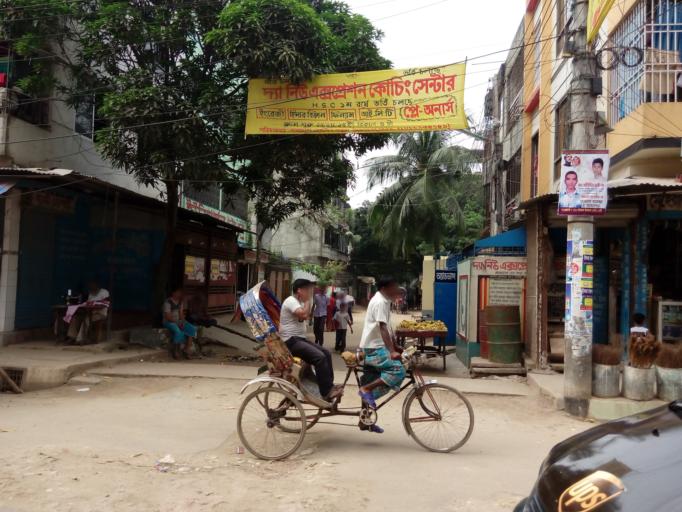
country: BD
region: Dhaka
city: Tungi
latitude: 23.8158
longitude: 90.3746
